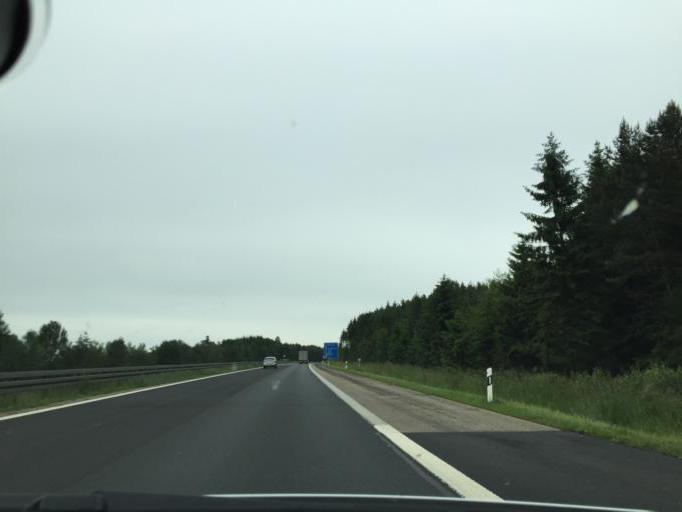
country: DE
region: Bavaria
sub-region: Regierungsbezirk Unterfranken
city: Bad Bruckenau
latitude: 50.3437
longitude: 9.7608
